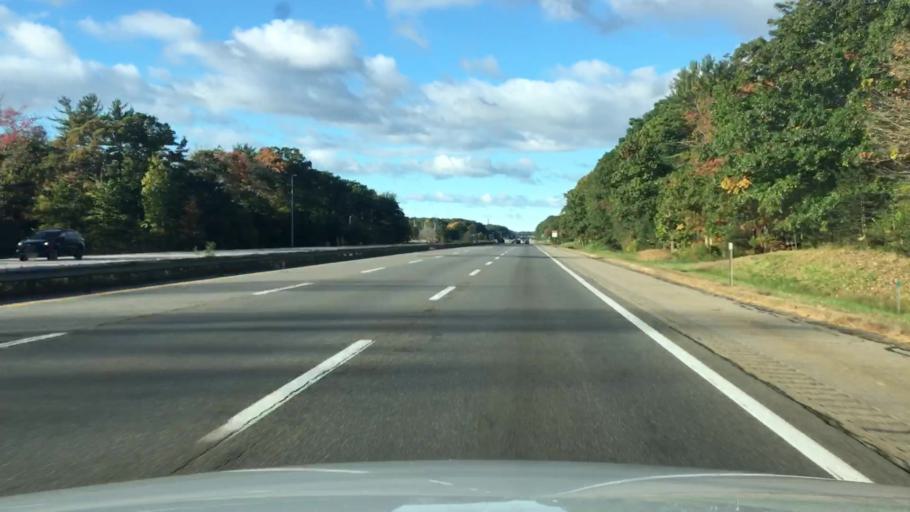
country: US
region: Maine
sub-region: York County
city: York Harbor
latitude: 43.1509
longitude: -70.6780
